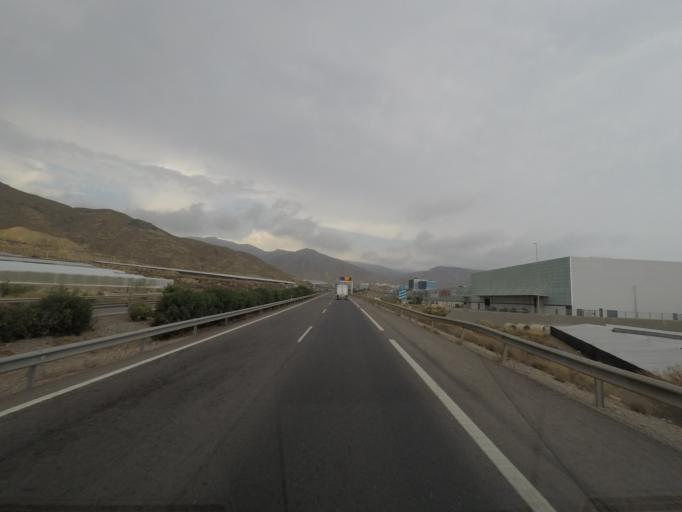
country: ES
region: Andalusia
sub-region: Provincia de Almeria
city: Aguadulce
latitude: 36.8155
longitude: -2.6045
